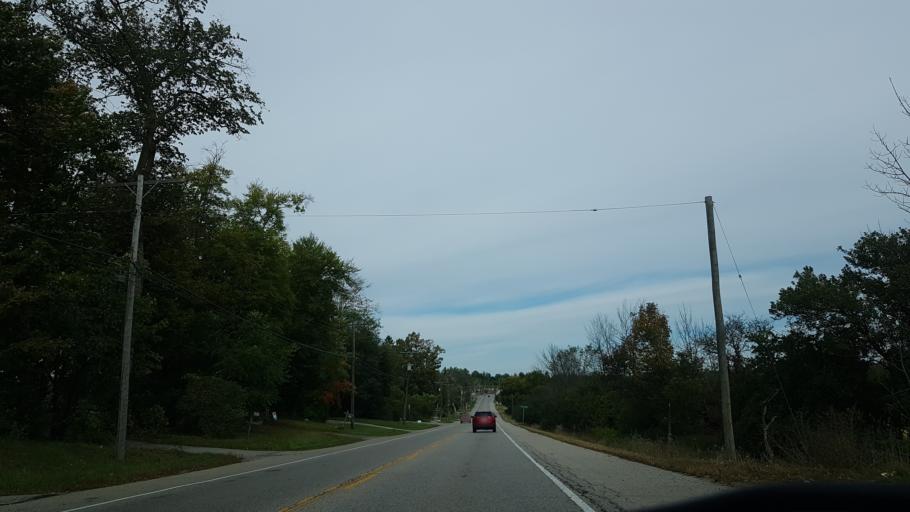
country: CA
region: Ontario
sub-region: Wellington County
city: Guelph
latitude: 43.5134
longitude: -80.2672
